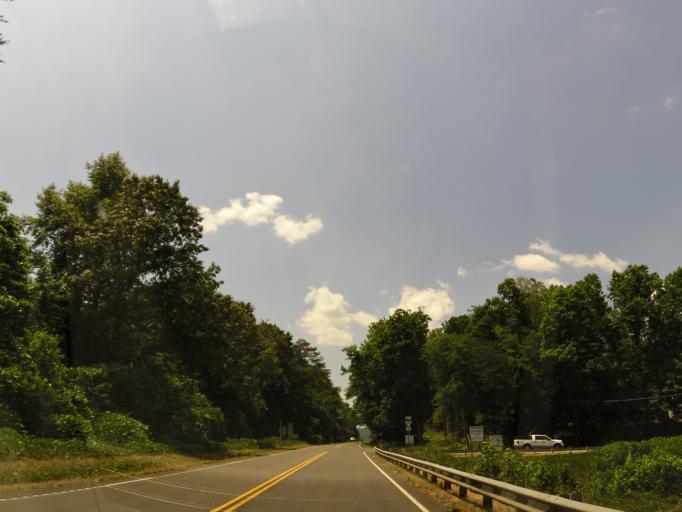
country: US
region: Tennessee
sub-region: Rhea County
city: Spring City
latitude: 35.6478
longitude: -84.8630
